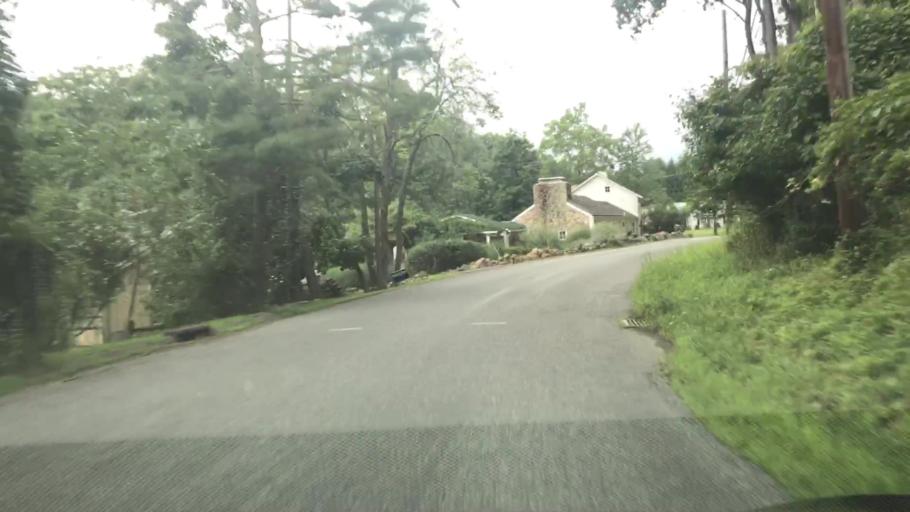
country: US
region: New Jersey
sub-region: Hunterdon County
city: Lebanon
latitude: 40.6686
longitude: -74.8531
